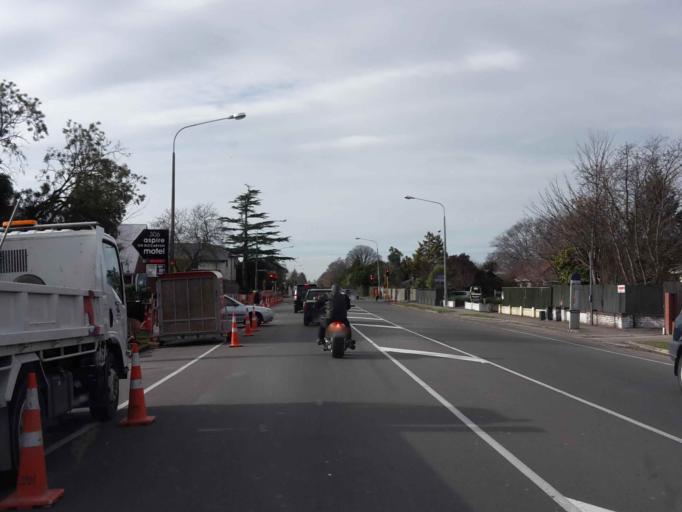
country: NZ
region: Canterbury
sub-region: Christchurch City
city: Christchurch
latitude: -43.5314
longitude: 172.5784
